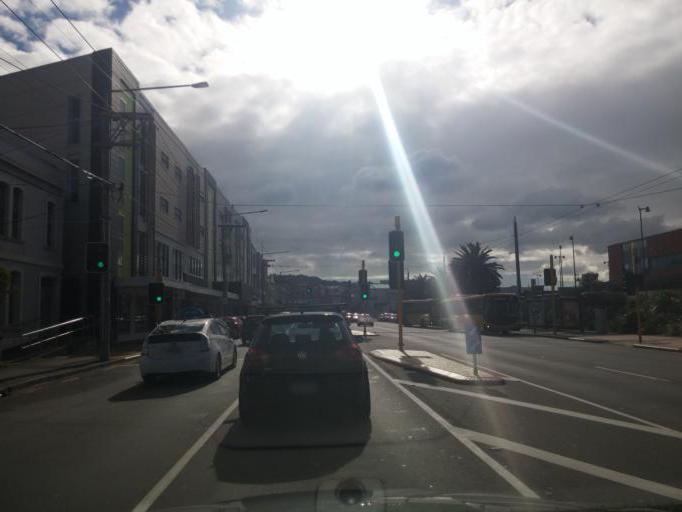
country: NZ
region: Wellington
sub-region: Wellington City
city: Wellington
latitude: -41.3095
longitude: 174.7787
